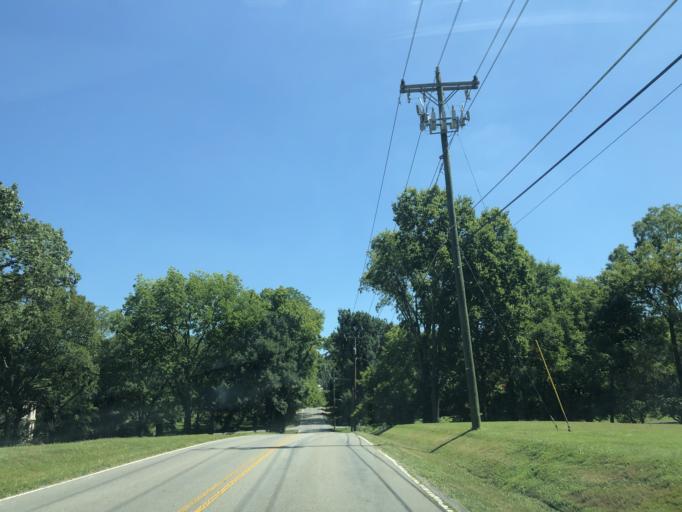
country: US
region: Tennessee
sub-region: Davidson County
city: Oak Hill
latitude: 36.0807
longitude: -86.8008
